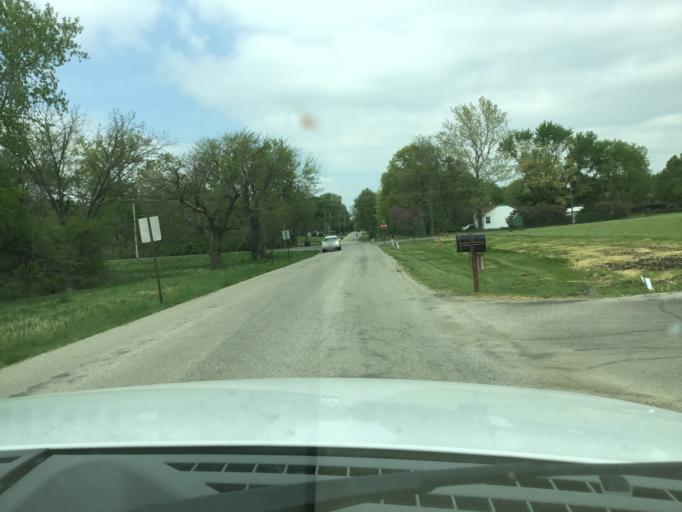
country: US
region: Kansas
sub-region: Shawnee County
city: Topeka
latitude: 39.0142
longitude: -95.5860
